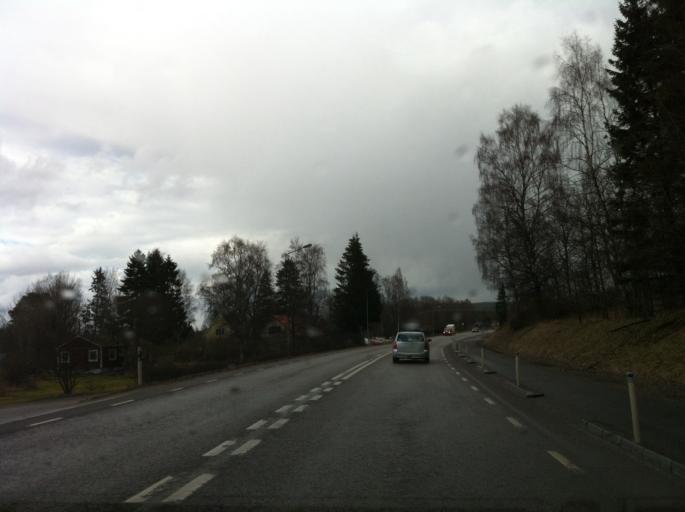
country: SE
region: Vaestra Goetaland
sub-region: Ulricehamns Kommun
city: Ulricehamn
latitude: 57.7502
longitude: 13.4224
